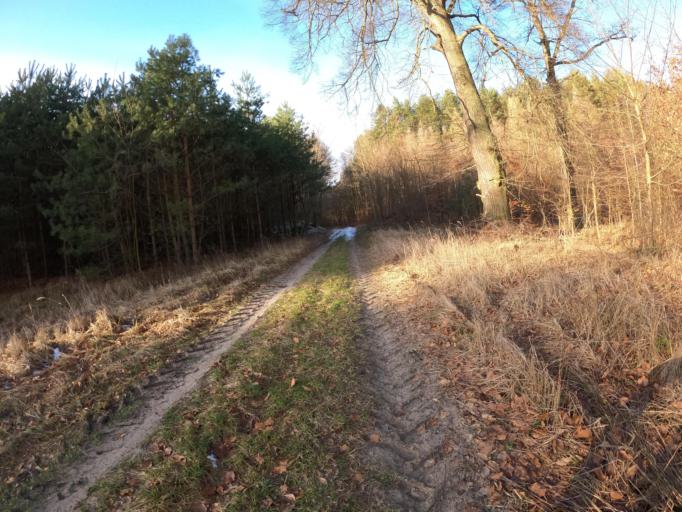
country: PL
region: Lubusz
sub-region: Powiat slubicki
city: Cybinka
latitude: 52.2206
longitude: 14.8349
